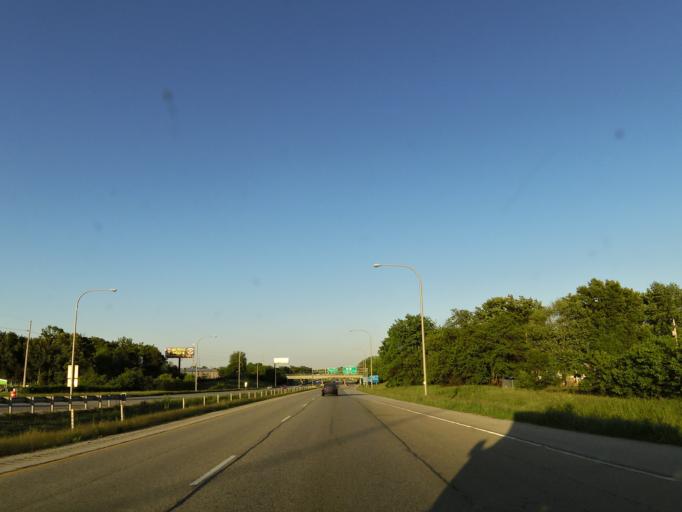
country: US
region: Illinois
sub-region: Vermilion County
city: Tilton
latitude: 40.1048
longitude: -87.6444
